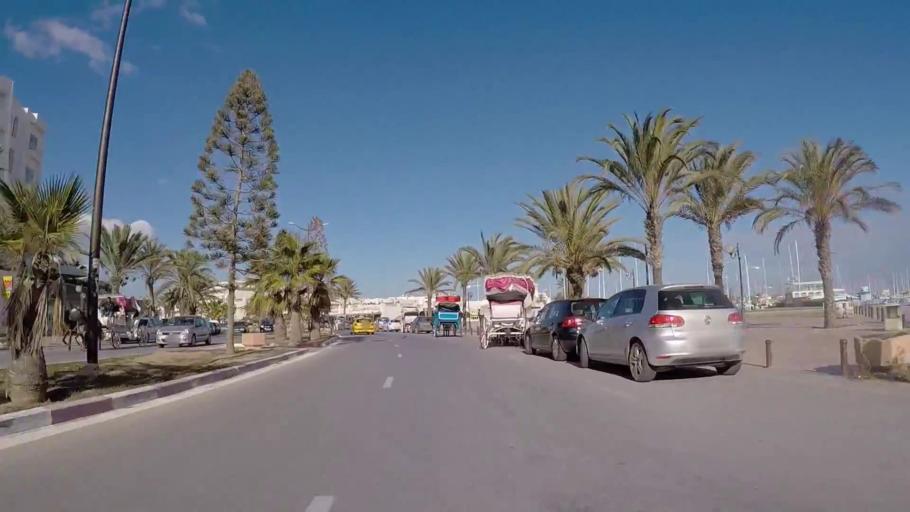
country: TN
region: Nabul
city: Al Hammamat
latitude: 36.3697
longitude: 10.5407
